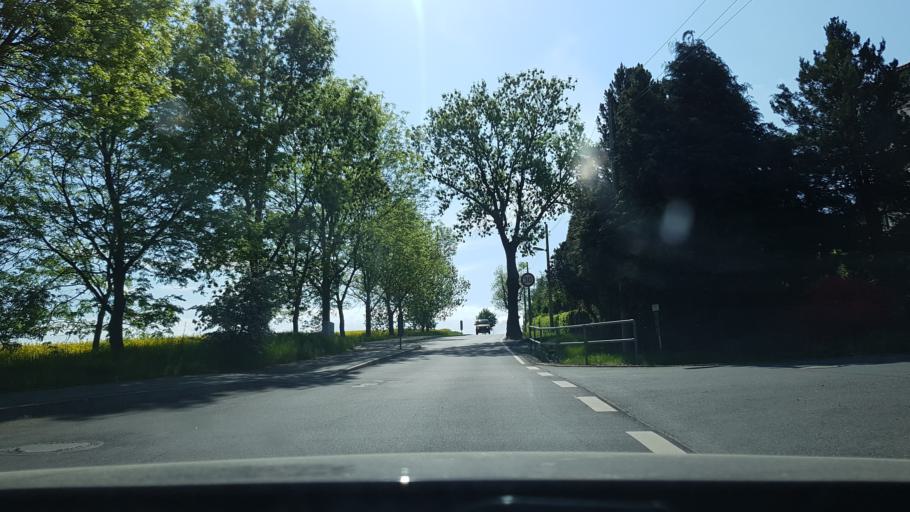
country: DE
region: Saxony
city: Wittgensdorf
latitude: 50.8664
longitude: 12.8825
